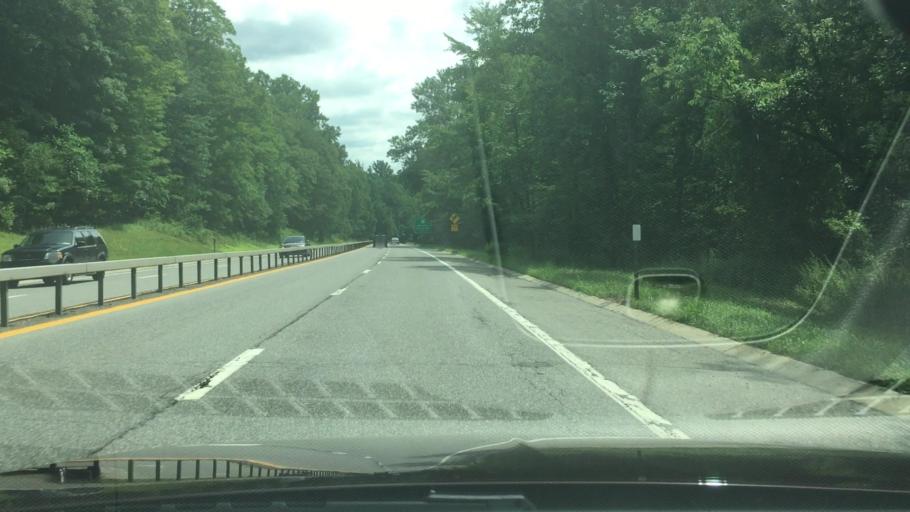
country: US
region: New York
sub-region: Westchester County
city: Shrub Oak
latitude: 41.3460
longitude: -73.8124
